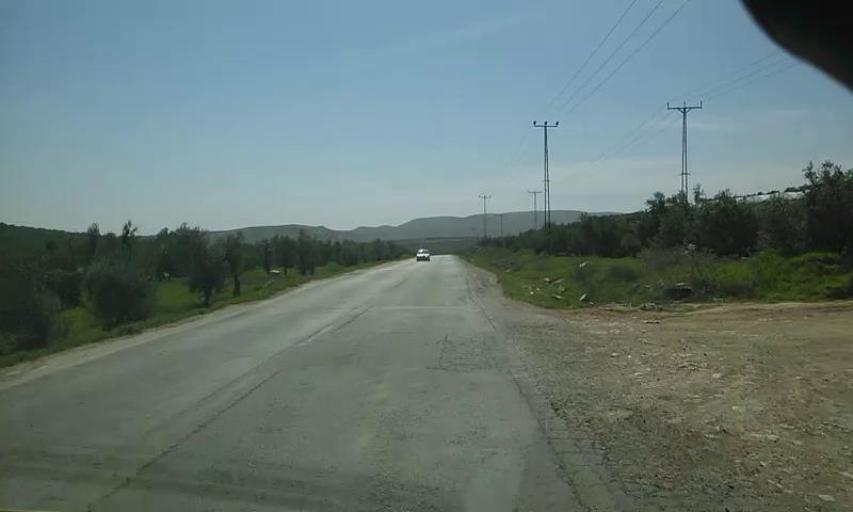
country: PS
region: West Bank
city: Marah Rabbah
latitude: 31.6369
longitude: 35.2026
